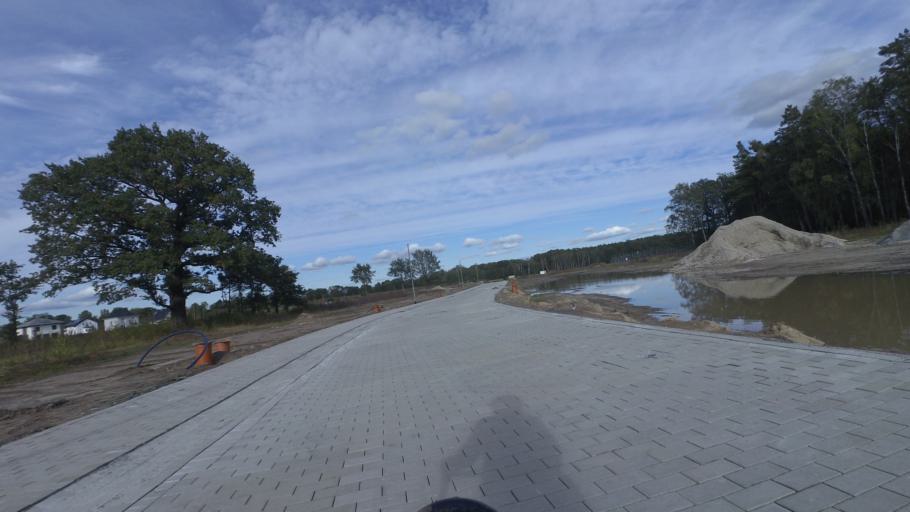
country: DE
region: Brandenburg
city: Ludwigsfelde
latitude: 52.3132
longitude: 13.2251
